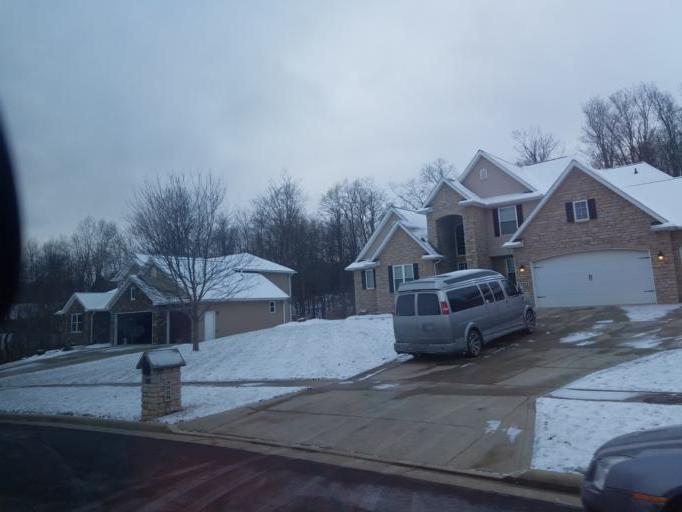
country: US
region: Ohio
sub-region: Richland County
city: Ontario
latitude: 40.7546
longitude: -82.6577
